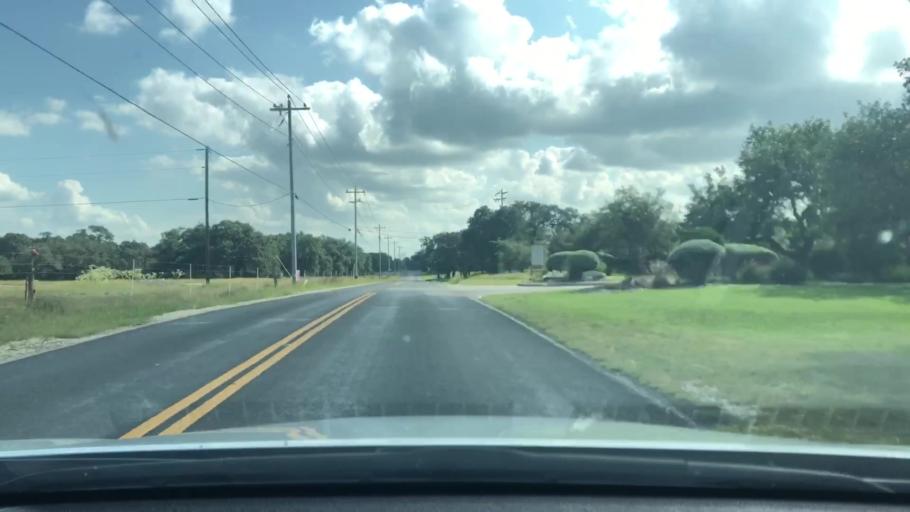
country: US
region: Texas
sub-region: Bexar County
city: Fair Oaks Ranch
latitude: 29.7761
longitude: -98.6264
